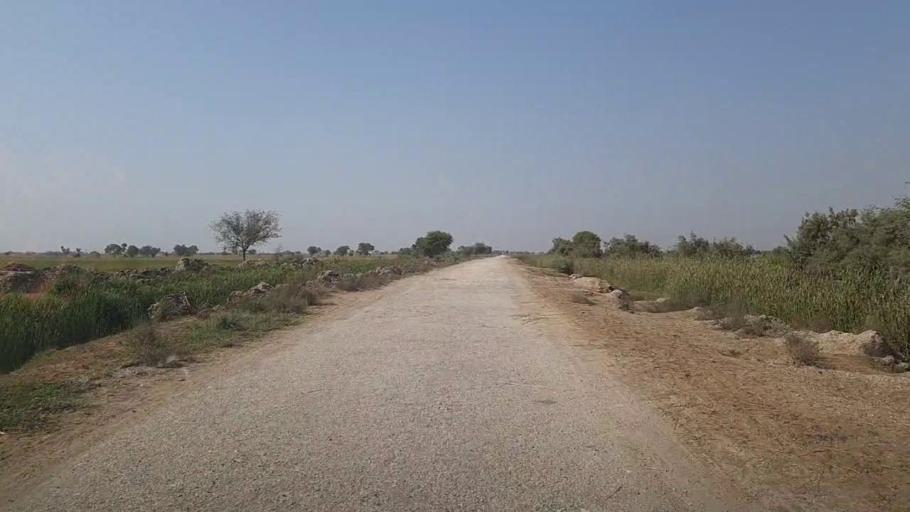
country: PK
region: Sindh
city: Kandhkot
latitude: 28.3952
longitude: 69.2740
